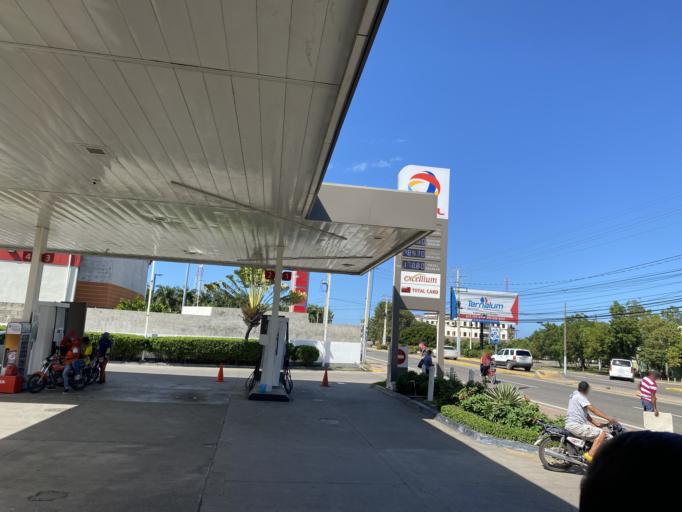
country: DO
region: Puerto Plata
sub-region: Puerto Plata
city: Puerto Plata
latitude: 19.7819
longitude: -70.6723
